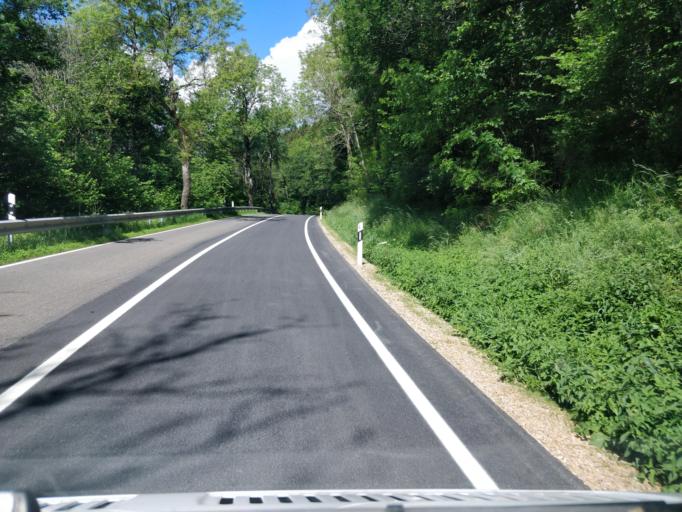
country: DE
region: Rheinland-Pfalz
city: Hallschlag
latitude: 50.3637
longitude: 6.4588
